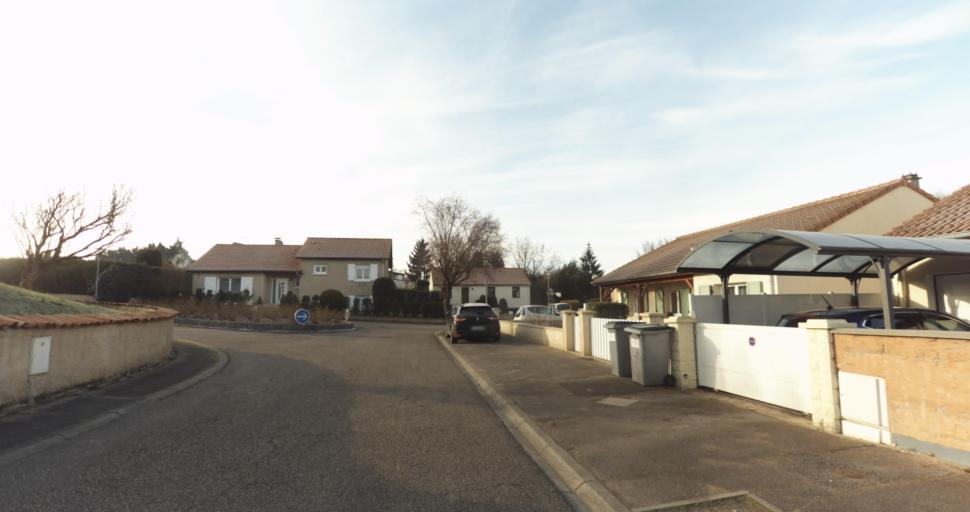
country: FR
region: Lorraine
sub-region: Departement de Meurthe-et-Moselle
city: Labry
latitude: 49.1660
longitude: 5.8843
